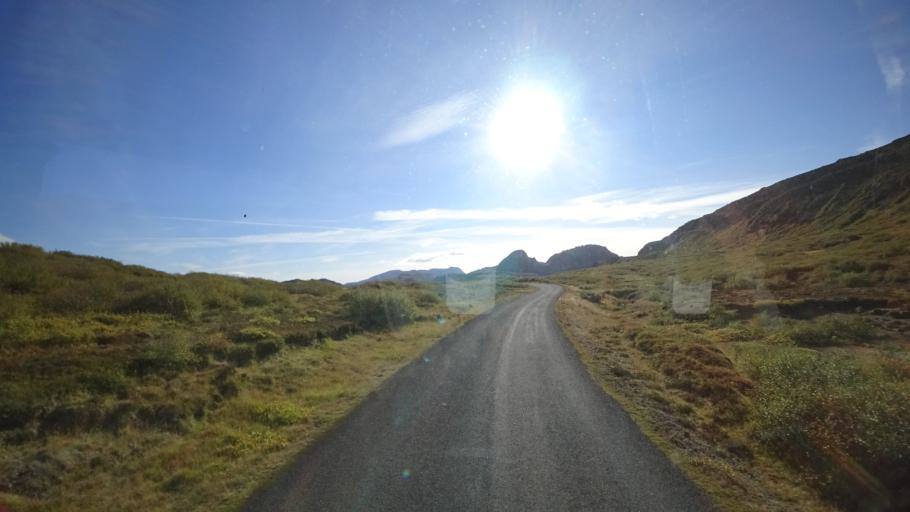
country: IS
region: South
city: Hveragerdi
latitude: 64.1601
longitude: -21.2475
